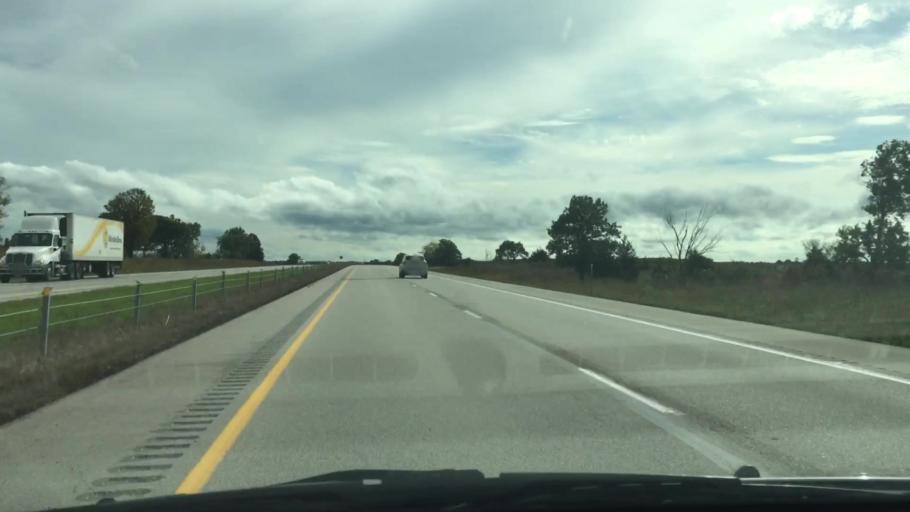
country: US
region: Iowa
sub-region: Clarke County
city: Osceola
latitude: 41.1217
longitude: -93.7818
